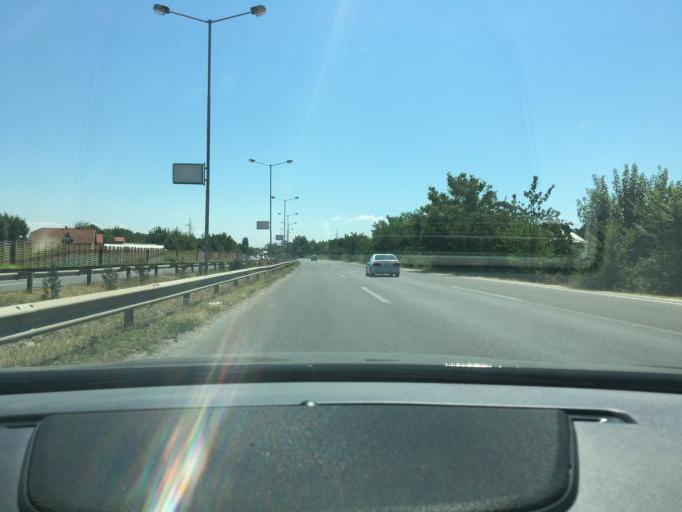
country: MK
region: Kisela Voda
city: Kisela Voda
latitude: 41.9992
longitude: 21.5016
